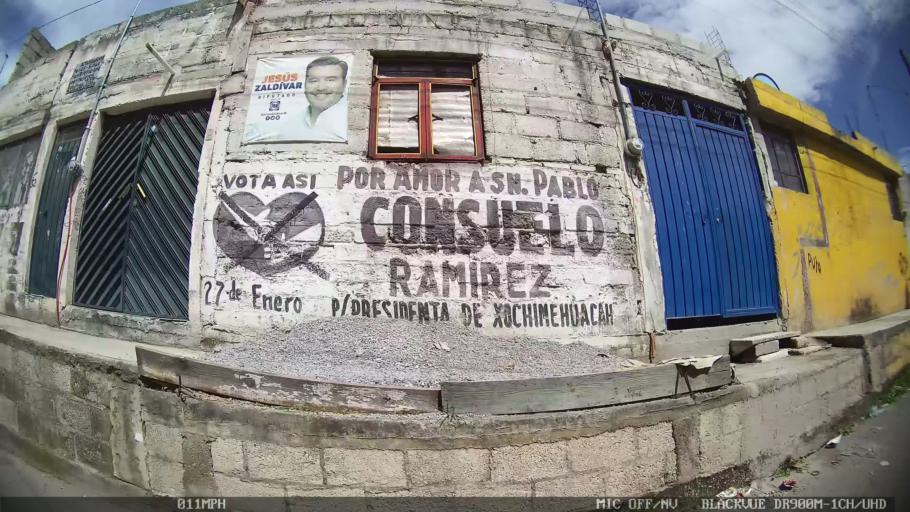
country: MX
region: Puebla
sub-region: Puebla
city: San Sebastian de Aparicio
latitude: 19.0906
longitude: -98.2046
